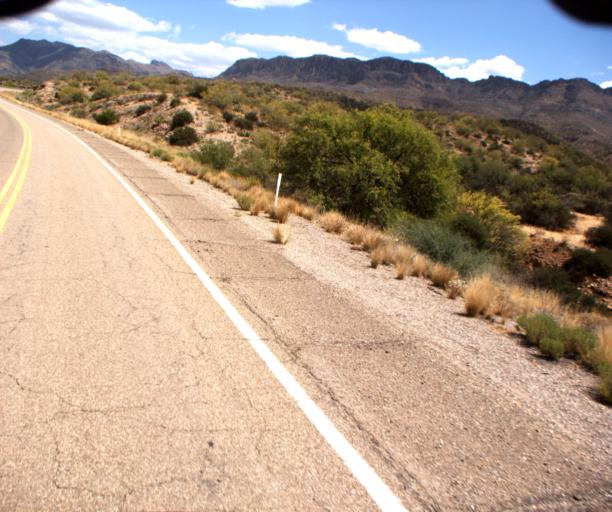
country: US
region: Arizona
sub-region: Pinal County
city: Superior
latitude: 33.2568
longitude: -111.0988
